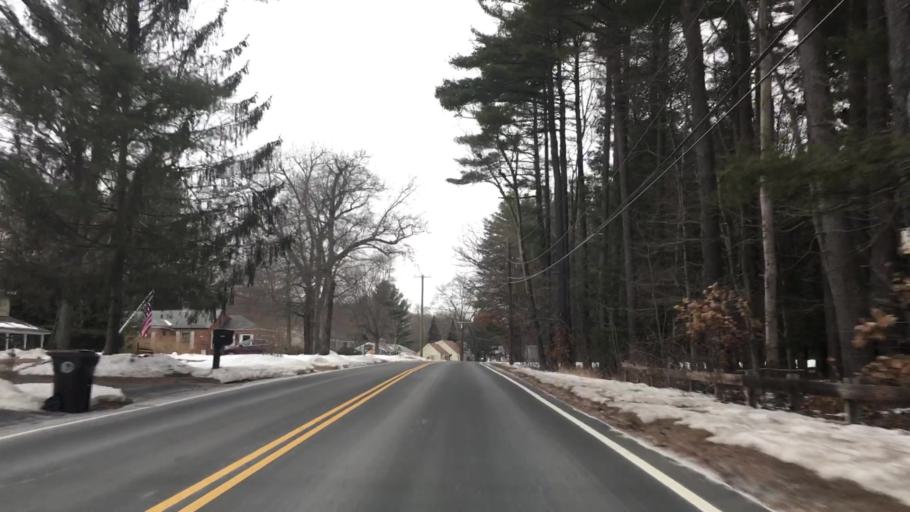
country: US
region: Massachusetts
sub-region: Hampden County
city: West Springfield
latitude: 42.0995
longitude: -72.6861
